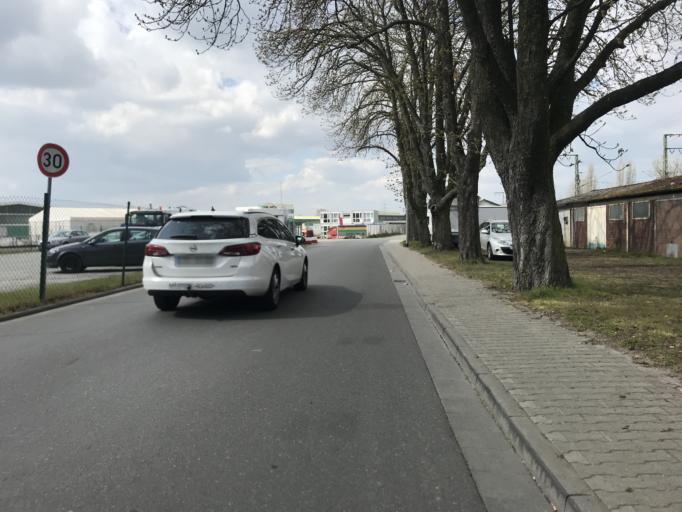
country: DE
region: Hesse
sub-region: Regierungsbezirk Darmstadt
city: Russelsheim
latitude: 50.0009
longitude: 8.3987
